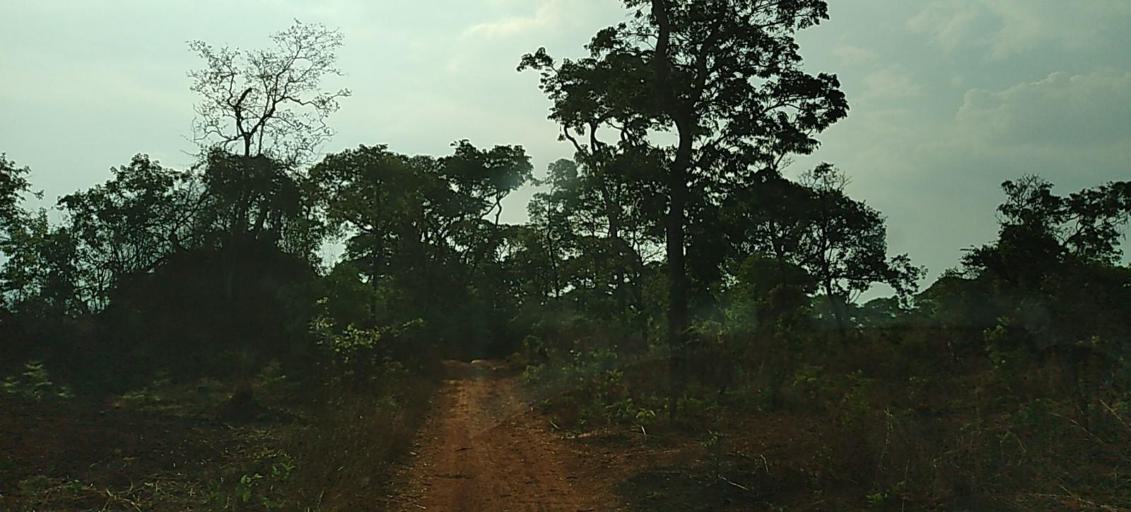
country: ZM
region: North-Western
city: Solwezi
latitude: -12.0555
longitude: 26.1563
